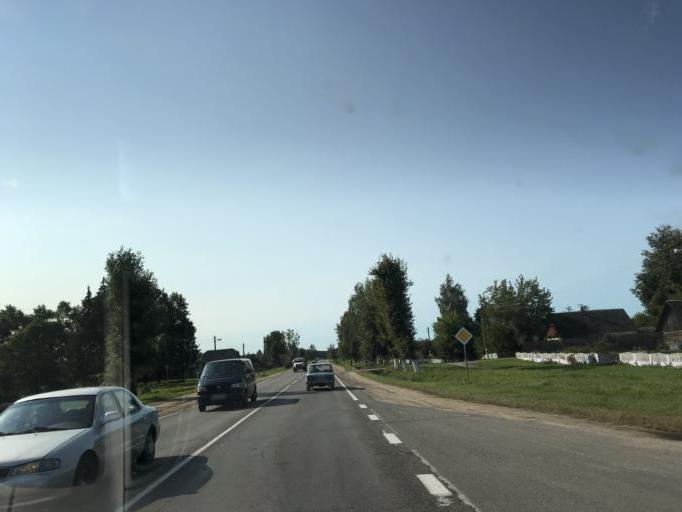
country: BY
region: Mogilev
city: Buynichy
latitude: 53.8304
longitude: 30.2437
